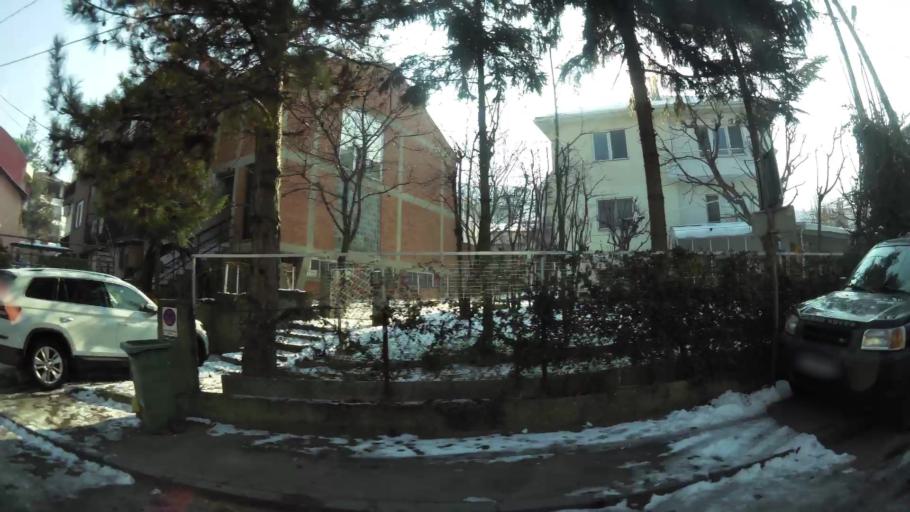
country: MK
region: Karpos
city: Skopje
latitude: 41.9852
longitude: 21.4199
